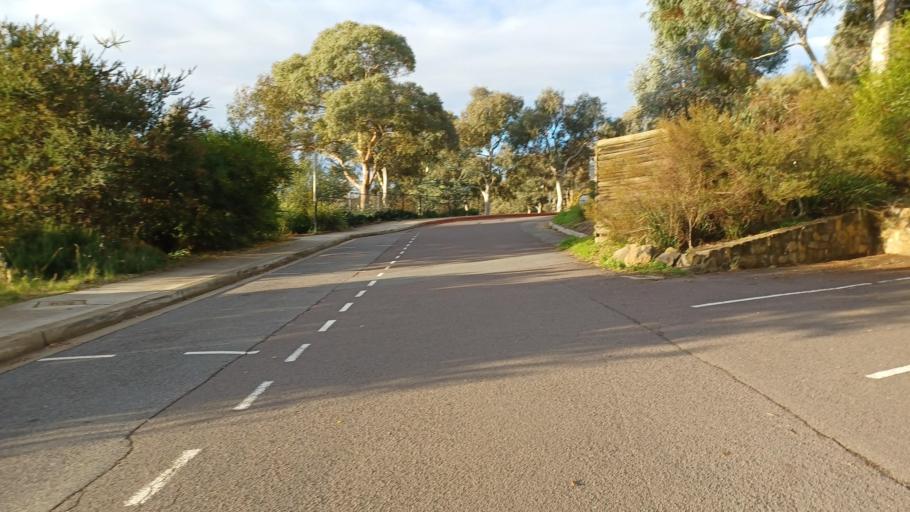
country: AU
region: Australian Capital Territory
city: Belconnen
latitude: -35.1919
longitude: 149.0436
